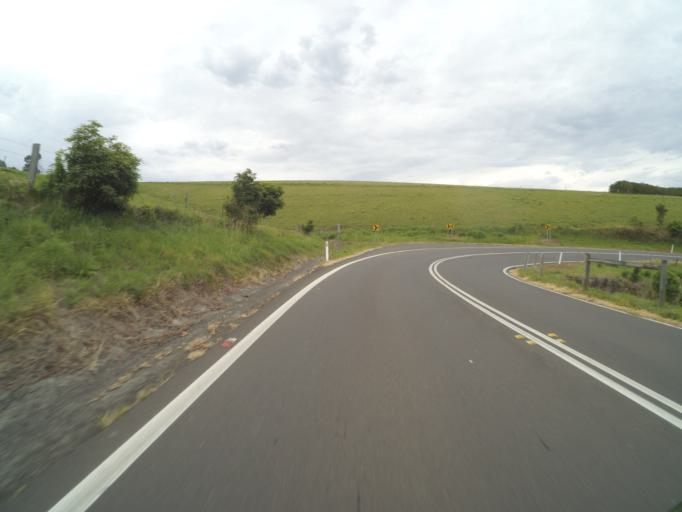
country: AU
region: New South Wales
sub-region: Kiama
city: Kiama
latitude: -34.6653
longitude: 150.8344
